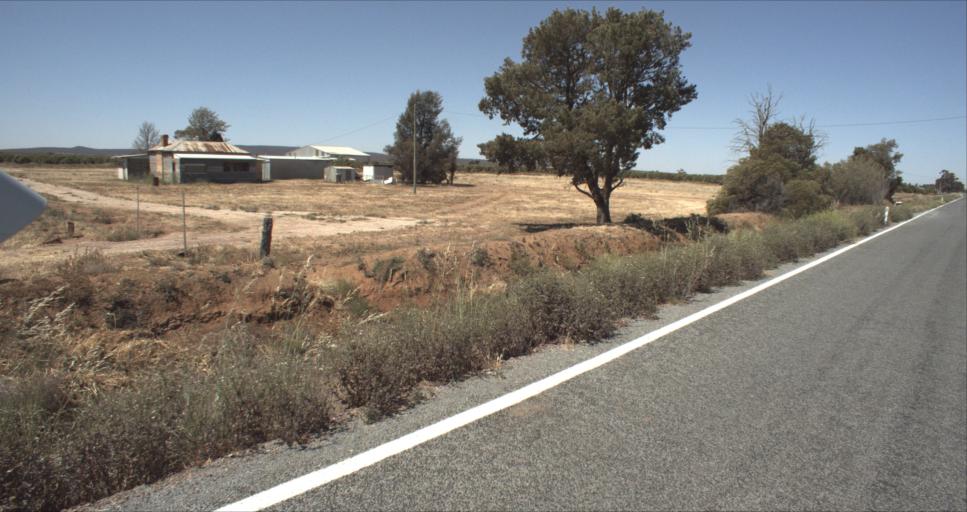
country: AU
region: New South Wales
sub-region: Leeton
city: Leeton
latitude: -34.5152
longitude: 146.4325
